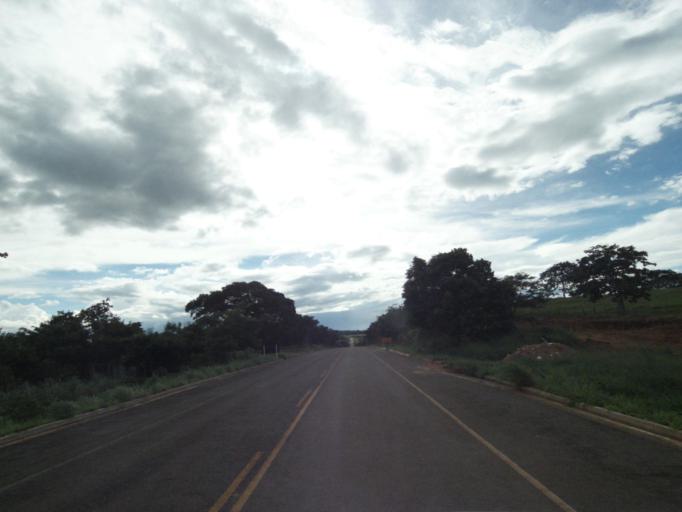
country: BR
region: Goias
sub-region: Jaragua
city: Jaragua
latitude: -15.8428
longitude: -49.3380
